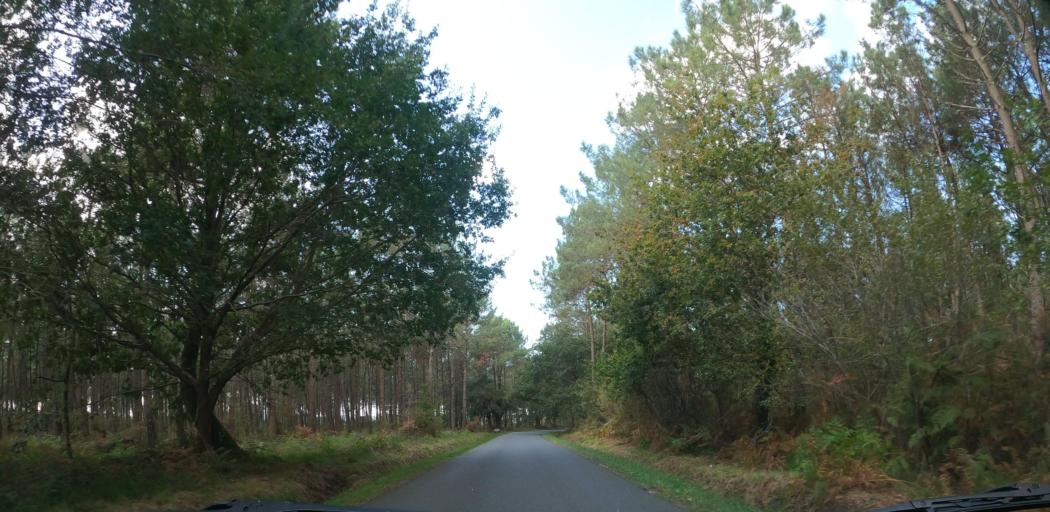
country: FR
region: Aquitaine
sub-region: Departement des Landes
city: Seignosse
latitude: 43.7156
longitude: -1.3553
